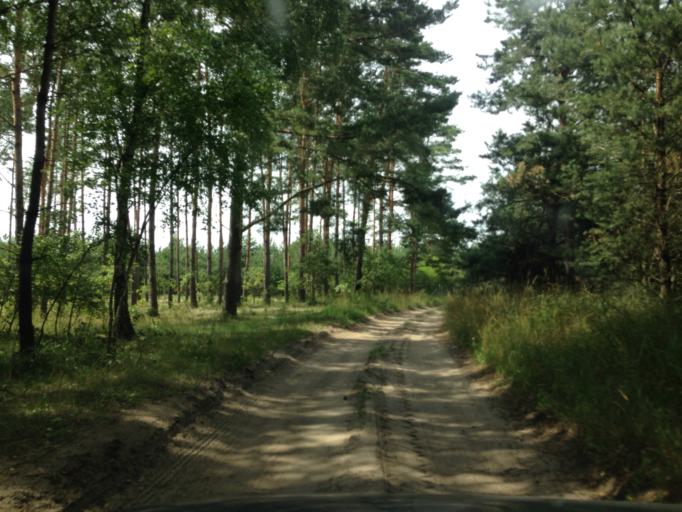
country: PL
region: Kujawsko-Pomorskie
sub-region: Powiat brodnicki
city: Bartniczka
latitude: 53.2735
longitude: 19.5114
